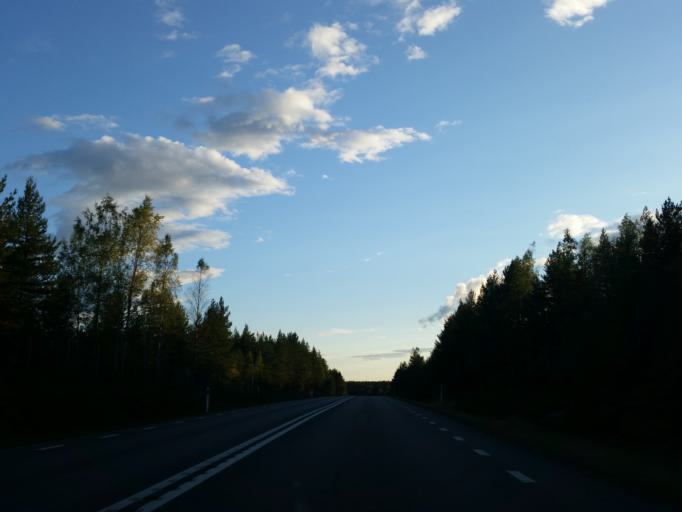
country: SE
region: Vaesterbotten
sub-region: Robertsfors Kommun
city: Robertsfors
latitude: 64.0163
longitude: 20.8287
